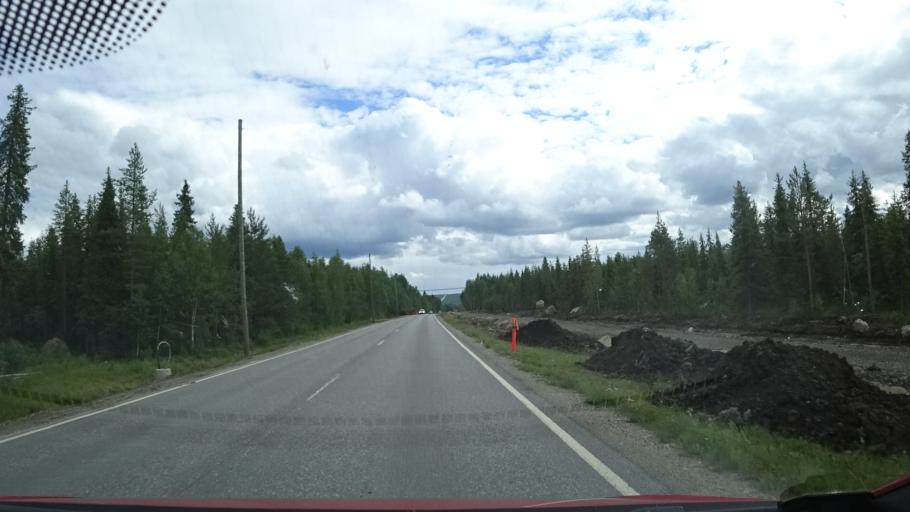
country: FI
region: Lapland
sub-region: Rovaniemi
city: Rovaniemi
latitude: 66.5351
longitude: 25.7292
